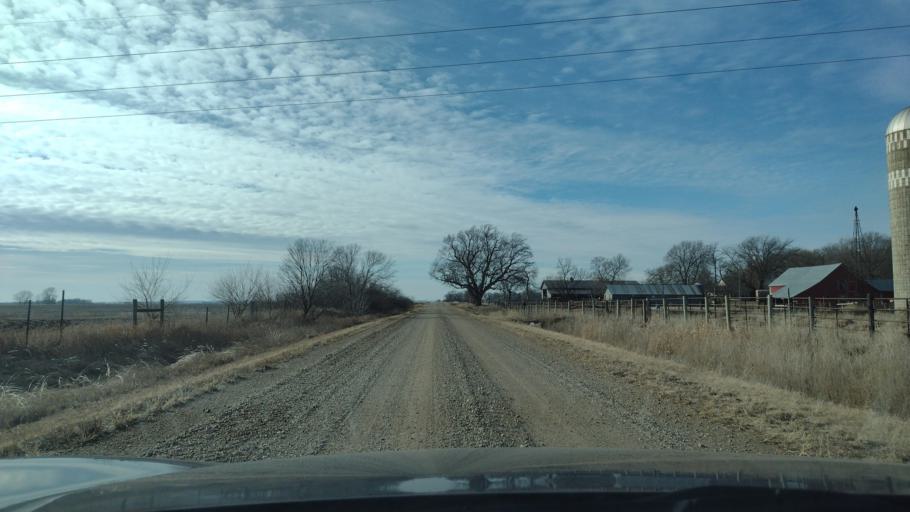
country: US
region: South Dakota
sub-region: Union County
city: Beresford
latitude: 42.9390
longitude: -96.8122
